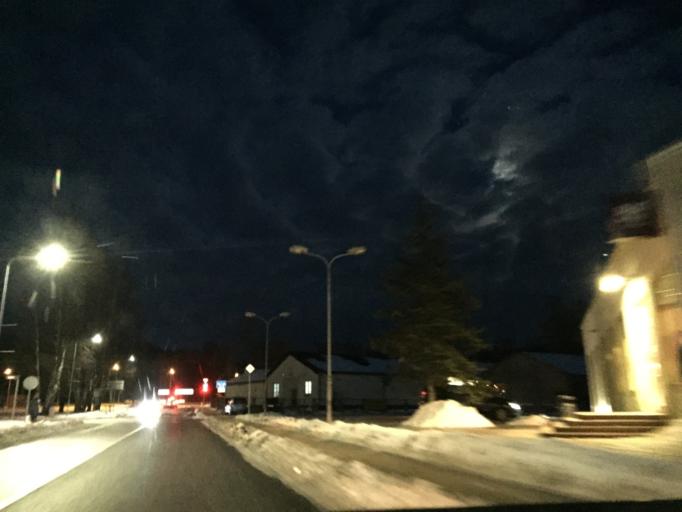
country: LV
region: Kegums
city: Kegums
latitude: 56.7438
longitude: 24.7192
